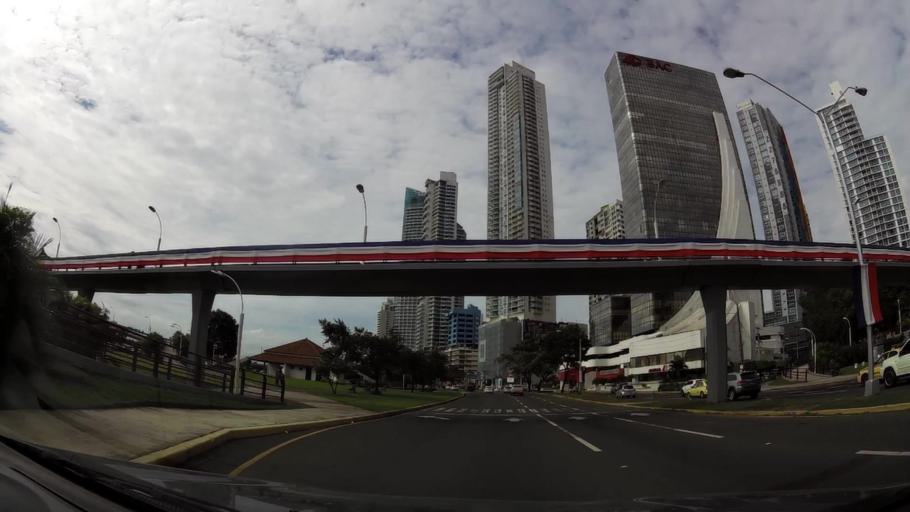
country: PA
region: Panama
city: Panama
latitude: 8.9746
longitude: -79.5276
